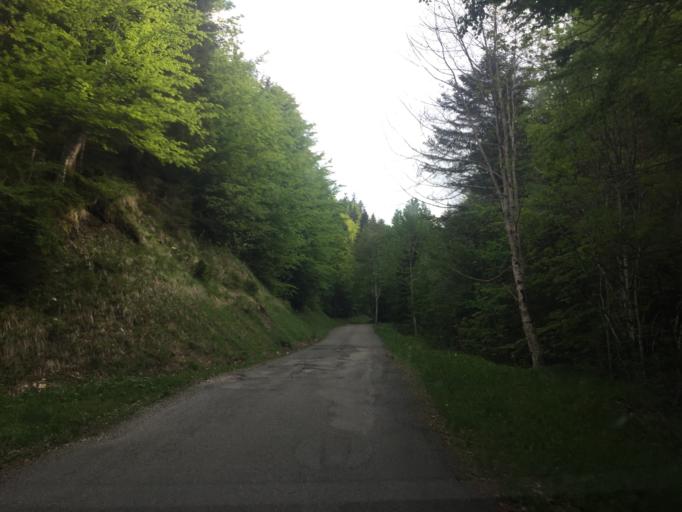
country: FR
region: Rhone-Alpes
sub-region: Departement de l'Isere
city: Le Sappey-en-Chartreuse
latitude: 45.2919
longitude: 5.8102
